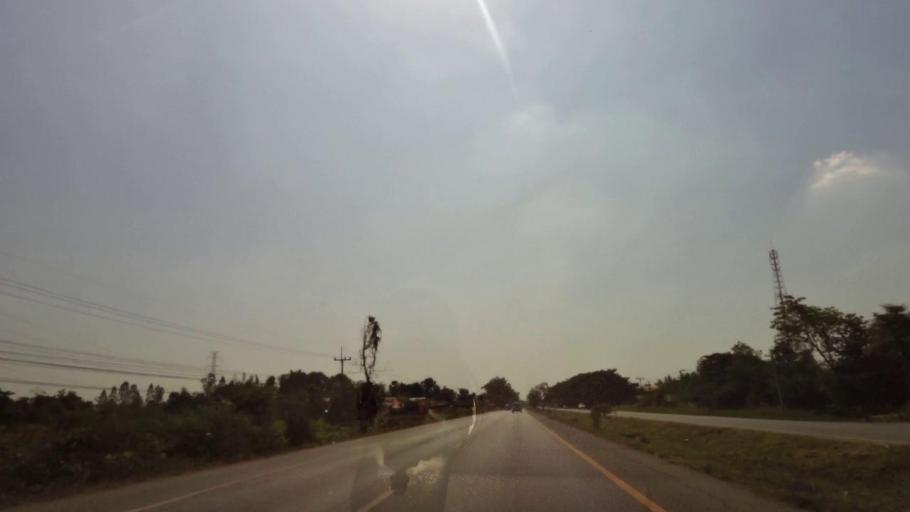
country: TH
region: Phichit
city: Wachira Barami
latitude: 16.3890
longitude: 100.1383
